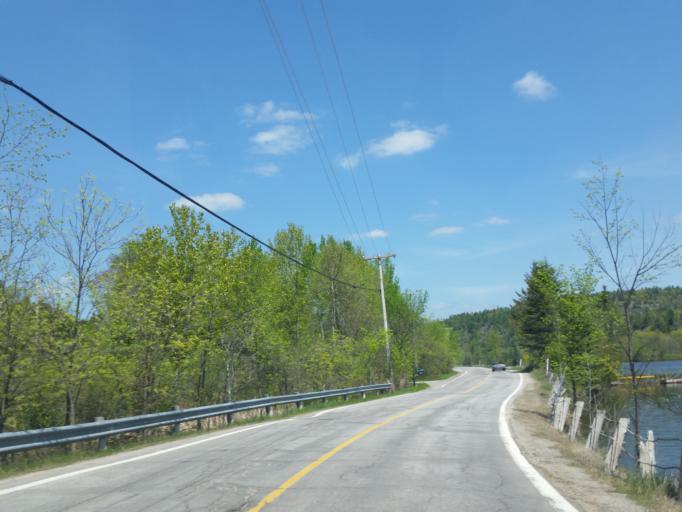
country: CA
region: Quebec
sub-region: Outaouais
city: Wakefield
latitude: 45.6101
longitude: -75.8980
